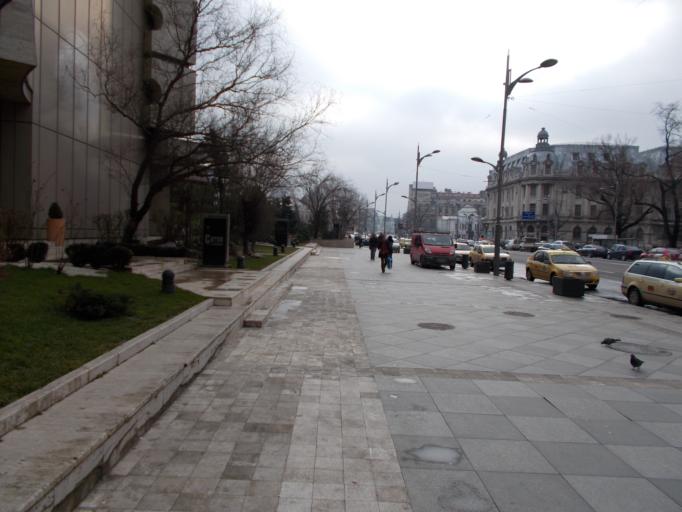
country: RO
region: Bucuresti
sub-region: Municipiul Bucuresti
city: Bucharest
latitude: 44.4371
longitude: 26.1019
